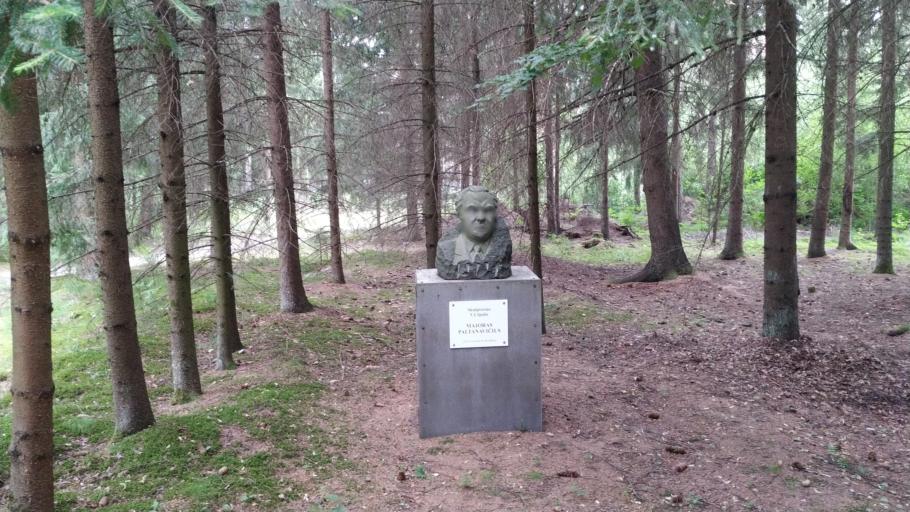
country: LT
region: Alytaus apskritis
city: Druskininkai
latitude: 54.0201
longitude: 24.0831
